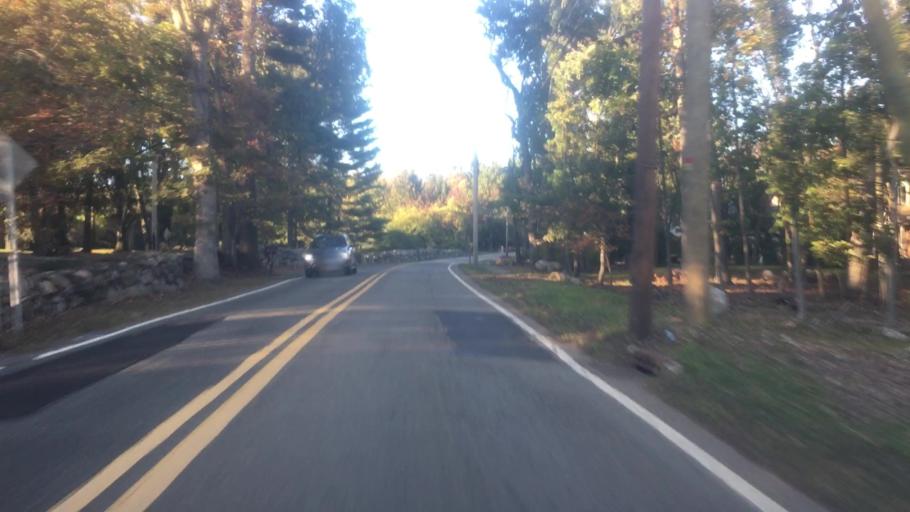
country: US
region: New Jersey
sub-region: Bergen County
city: Franklin Lakes
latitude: 40.9898
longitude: -74.1999
